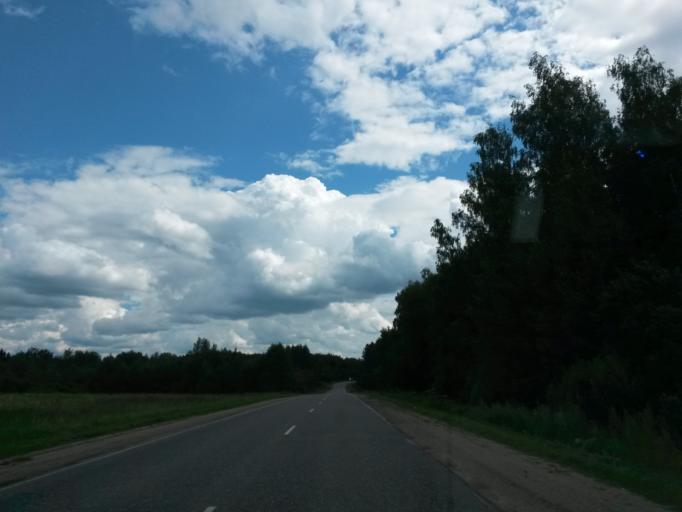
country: RU
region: Ivanovo
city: Pistsovo
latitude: 57.1196
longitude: 40.6340
